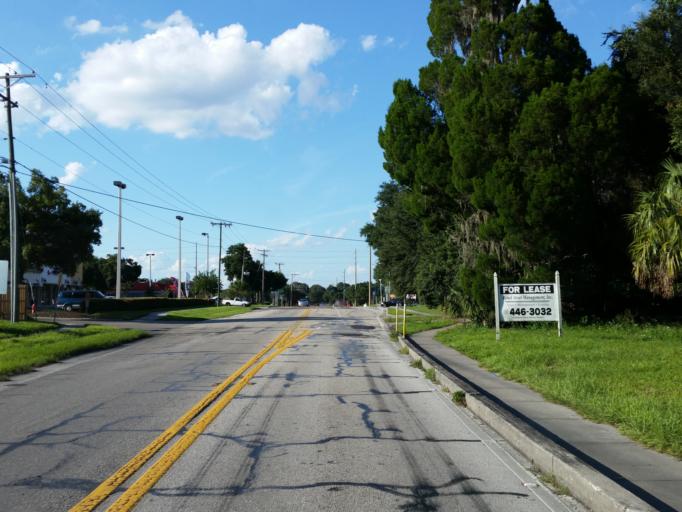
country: US
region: Florida
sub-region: Hillsborough County
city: Valrico
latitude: 27.9357
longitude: -82.2528
